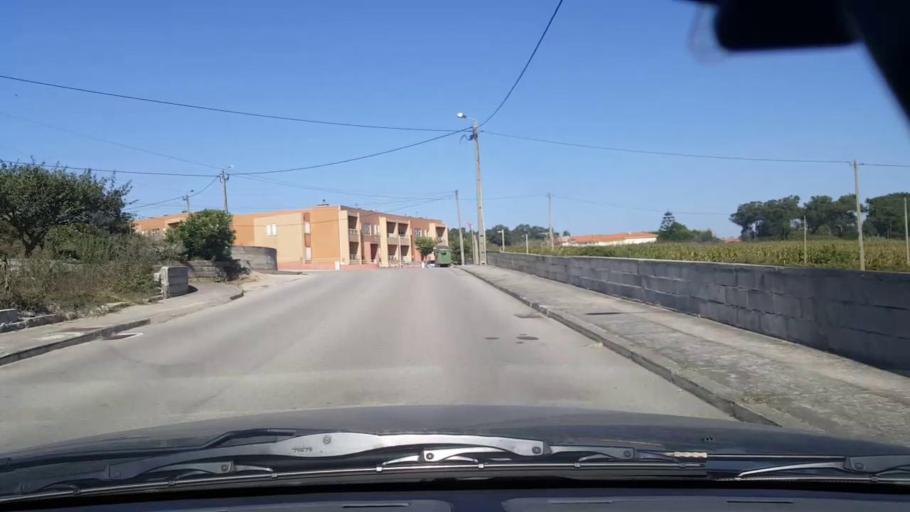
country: PT
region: Porto
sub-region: Matosinhos
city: Lavra
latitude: 41.2948
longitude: -8.7324
